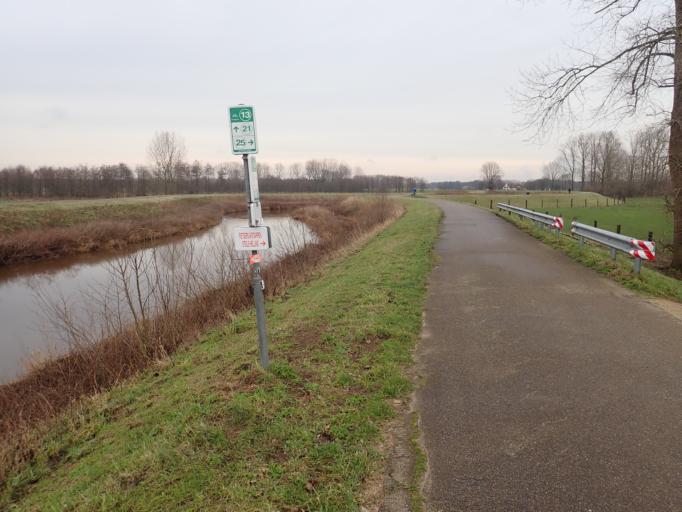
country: BE
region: Flanders
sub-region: Provincie Antwerpen
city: Nijlen
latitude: 51.1768
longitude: 4.6823
